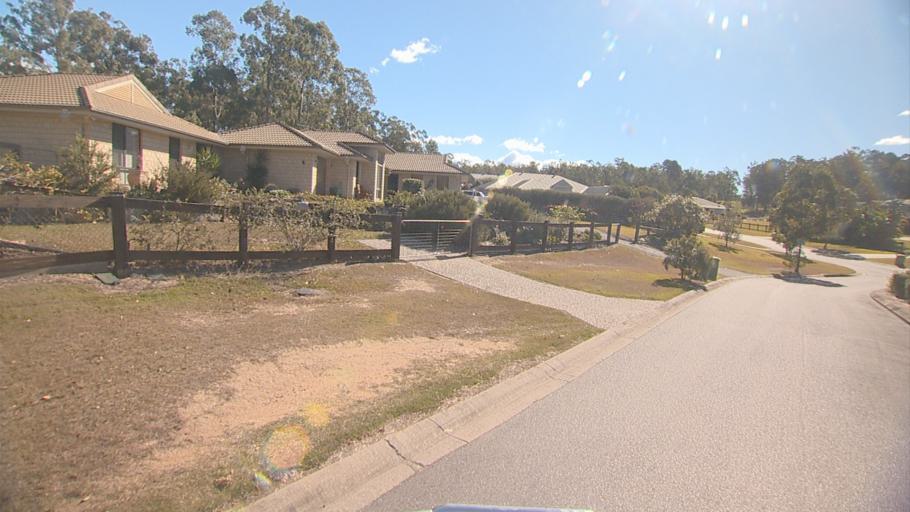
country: AU
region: Queensland
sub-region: Ipswich
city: Springfield Lakes
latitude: -27.7246
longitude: 152.9299
